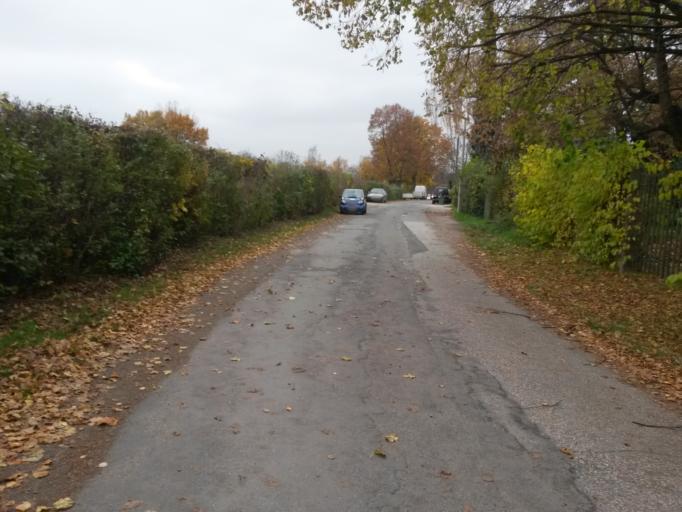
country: DE
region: Bavaria
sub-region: Regierungsbezirk Mittelfranken
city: Furth
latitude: 49.4730
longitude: 11.0127
